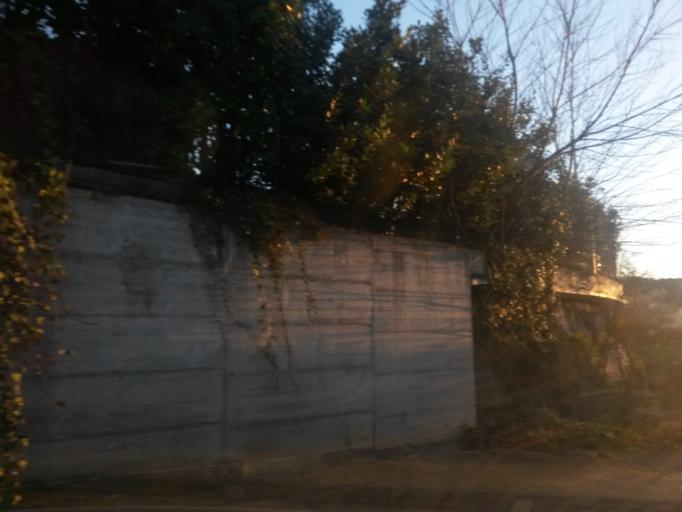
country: ES
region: Catalonia
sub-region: Provincia de Girona
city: Macanet de la Selva
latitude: 41.7932
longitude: 2.7259
